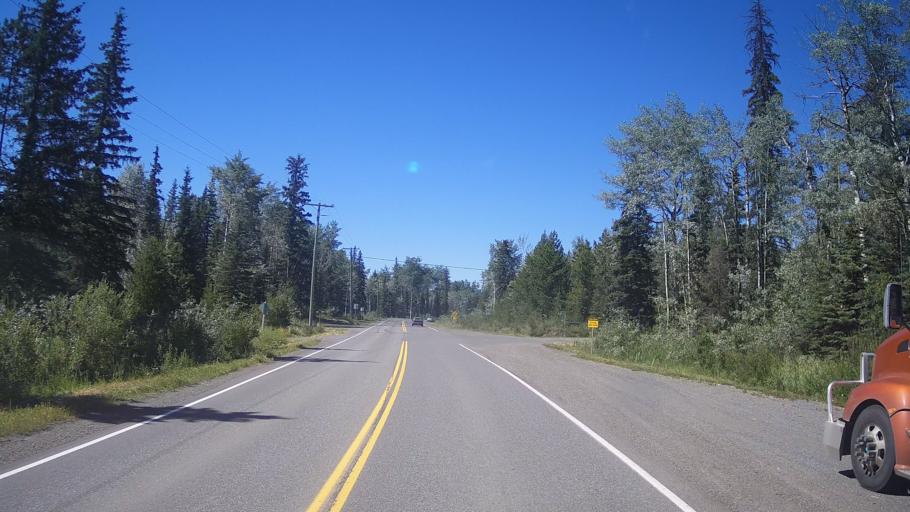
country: CA
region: British Columbia
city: Cache Creek
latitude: 51.5546
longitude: -121.2205
